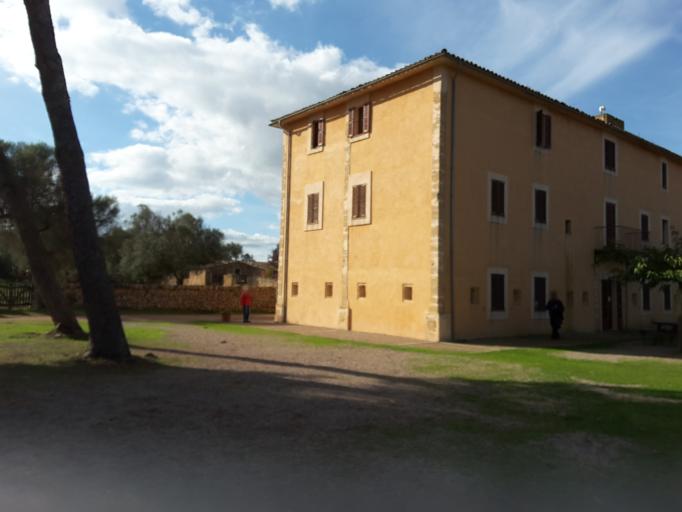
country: ES
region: Balearic Islands
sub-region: Illes Balears
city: Santa Margalida
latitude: 39.7367
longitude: 3.1834
